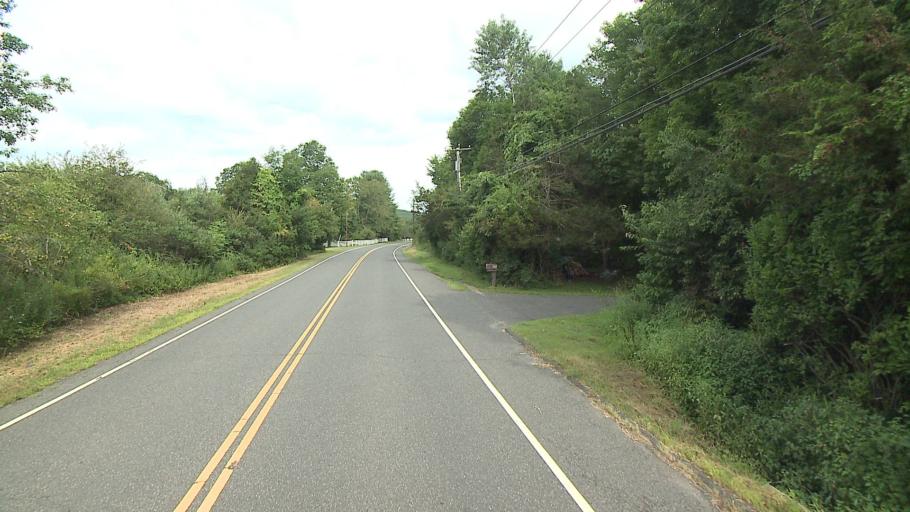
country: US
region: Connecticut
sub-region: Litchfield County
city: Woodbury
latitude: 41.5800
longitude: -73.2438
